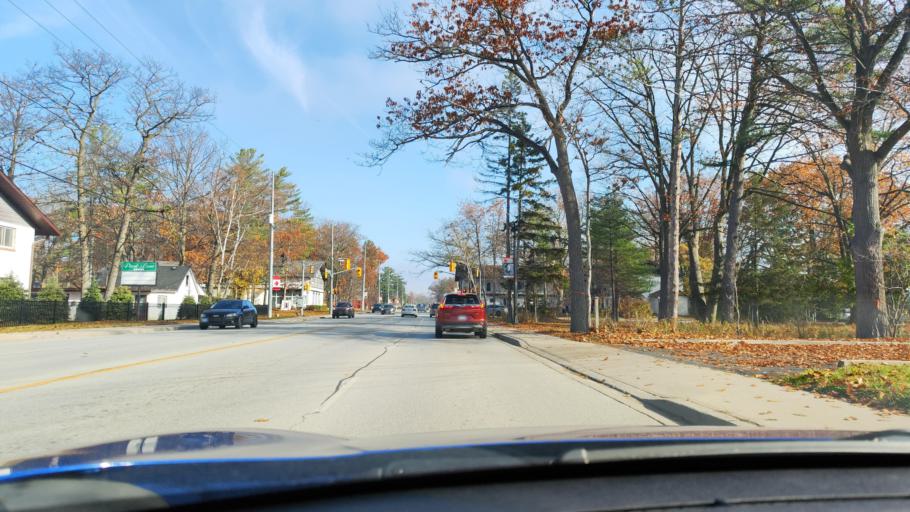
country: CA
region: Ontario
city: Wasaga Beach
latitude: 44.4856
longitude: -80.0570
